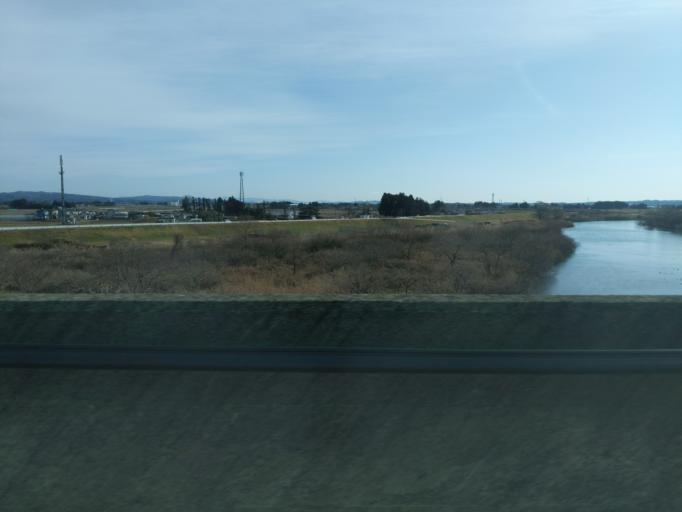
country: JP
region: Miyagi
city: Furukawa
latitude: 38.5876
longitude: 140.9737
